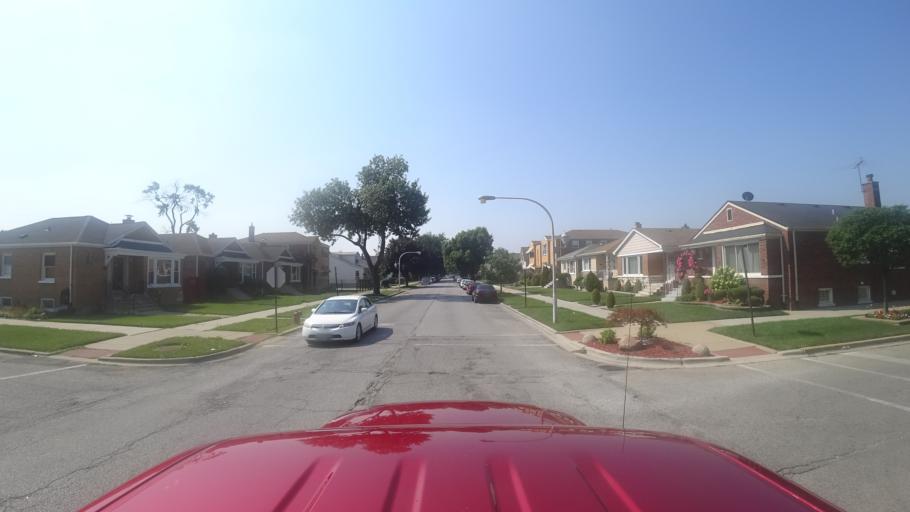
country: US
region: Illinois
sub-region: Cook County
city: Hometown
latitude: 41.7913
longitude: -87.7330
